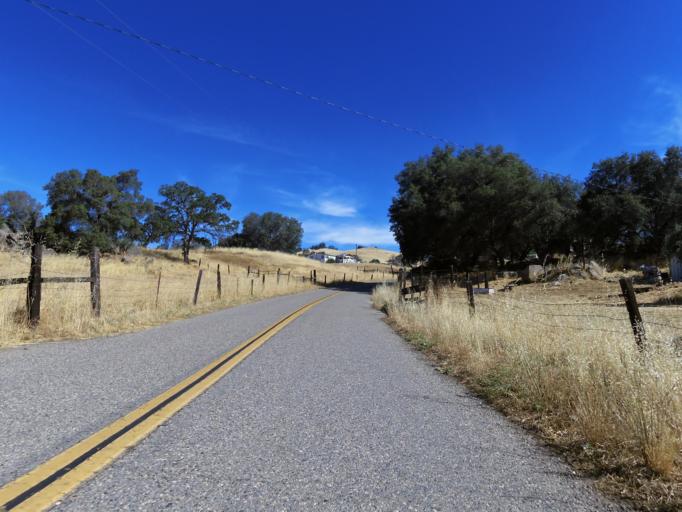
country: US
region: California
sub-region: Madera County
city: Yosemite Lakes
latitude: 37.2664
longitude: -119.9748
